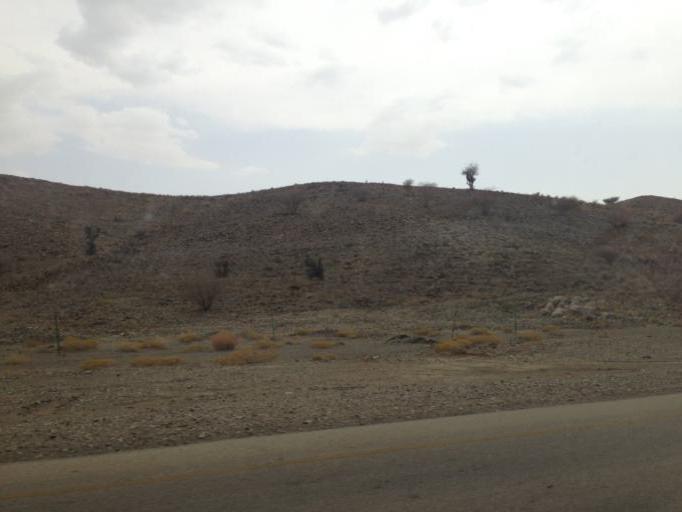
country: OM
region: Ash Sharqiyah
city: Badiyah
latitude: 22.5564
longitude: 59.0109
